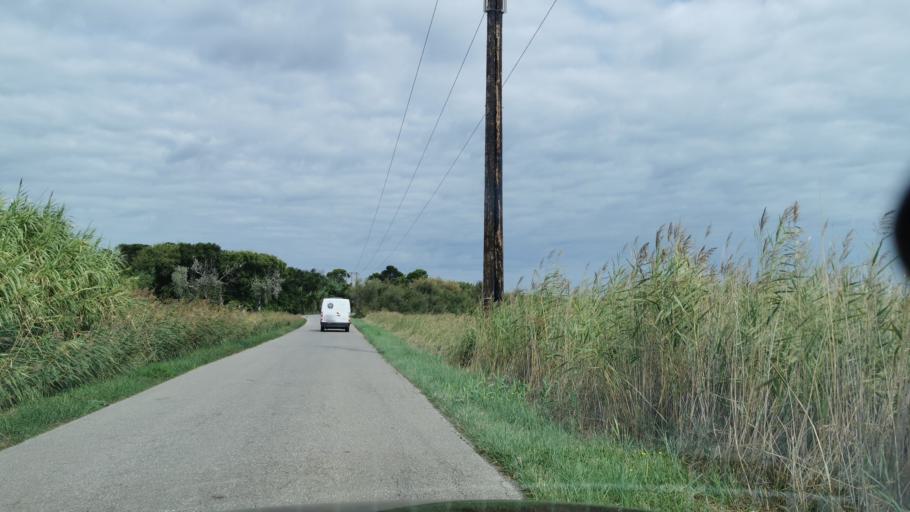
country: FR
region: Languedoc-Roussillon
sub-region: Departement de l'Aude
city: Fleury
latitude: 43.2021
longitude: 3.1912
